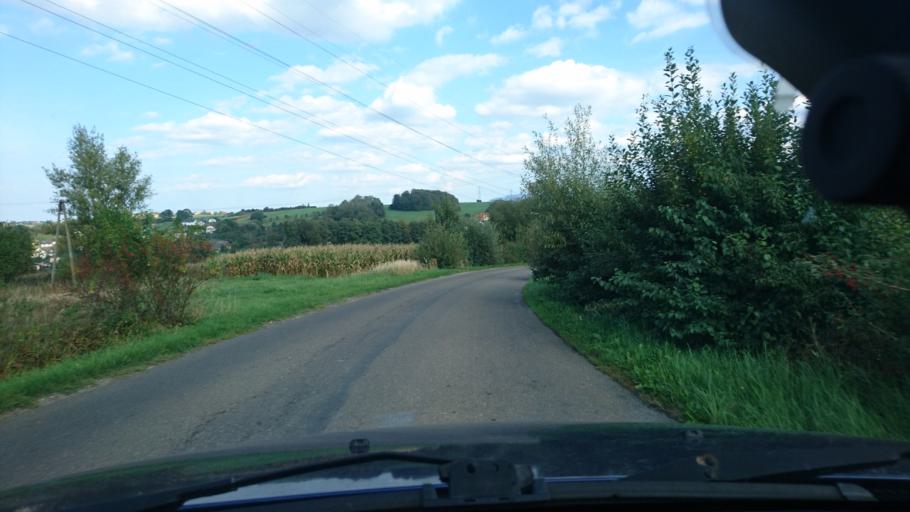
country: PL
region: Silesian Voivodeship
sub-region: Powiat bielski
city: Jasienica
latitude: 49.8314
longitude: 18.9352
